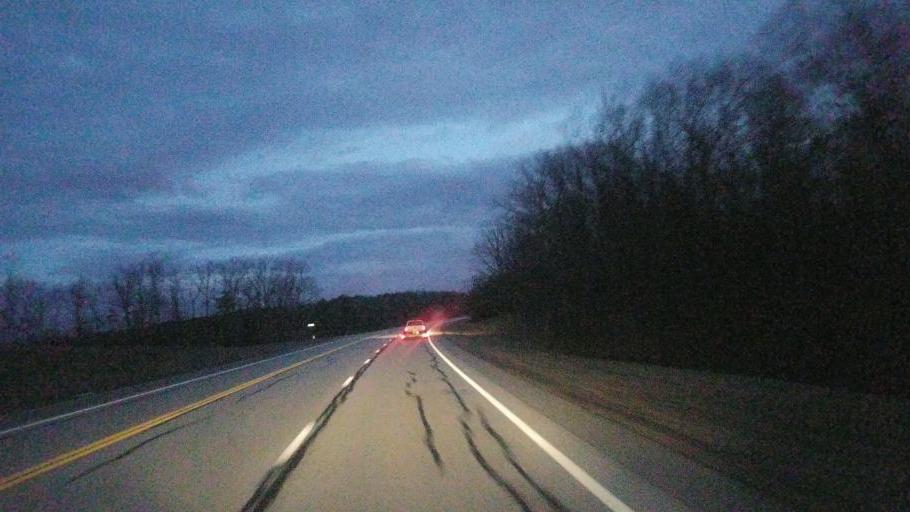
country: US
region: Tennessee
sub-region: Sequatchie County
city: Dunlap
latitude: 35.5045
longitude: -85.4745
